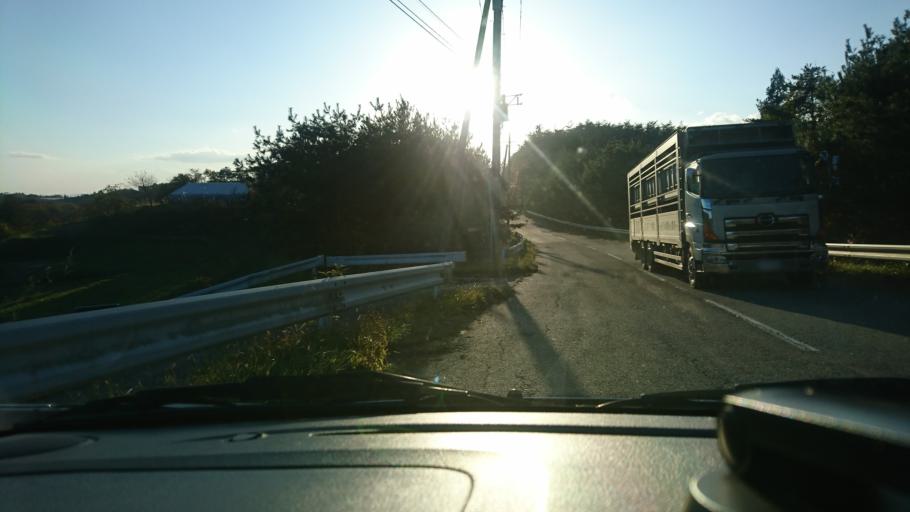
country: JP
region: Iwate
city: Ichinoseki
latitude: 38.8150
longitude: 141.2675
